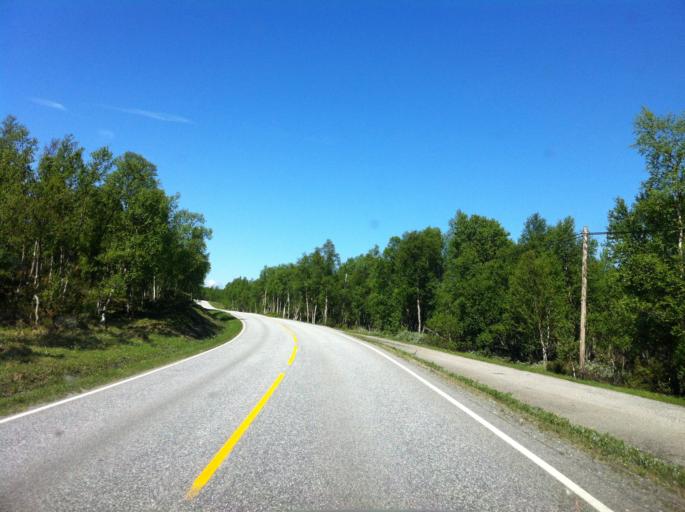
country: NO
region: Sor-Trondelag
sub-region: Roros
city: Roros
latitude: 62.5965
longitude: 11.7079
